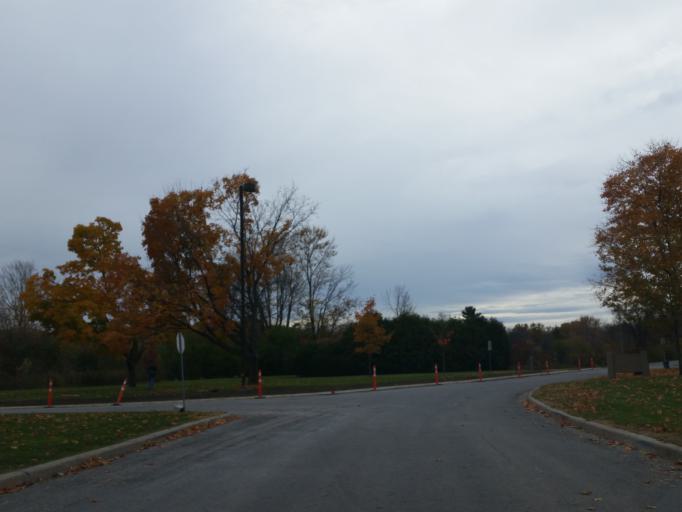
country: CA
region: Ontario
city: Bells Corners
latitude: 45.3742
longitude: -75.7947
